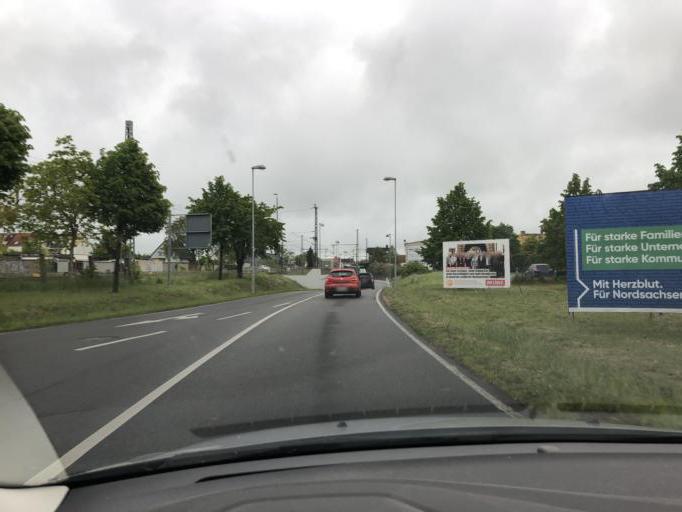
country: DE
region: Saxony
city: Delitzsch
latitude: 51.5293
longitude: 12.3423
